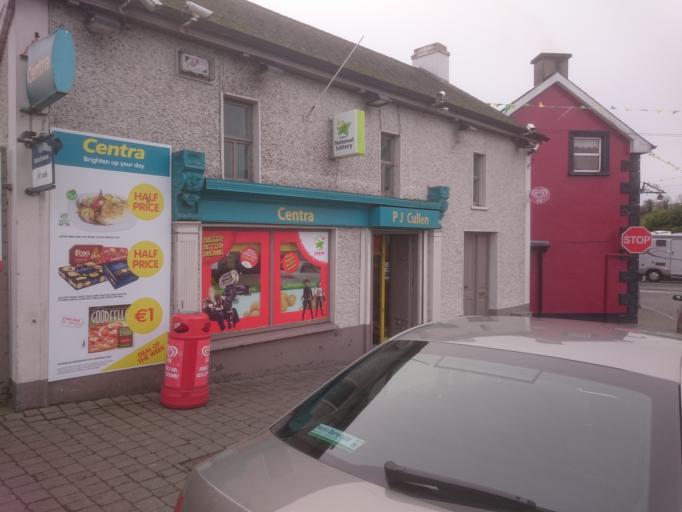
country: IE
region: Leinster
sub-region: Kilkenny
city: Thomastown
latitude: 52.5924
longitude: -7.1839
